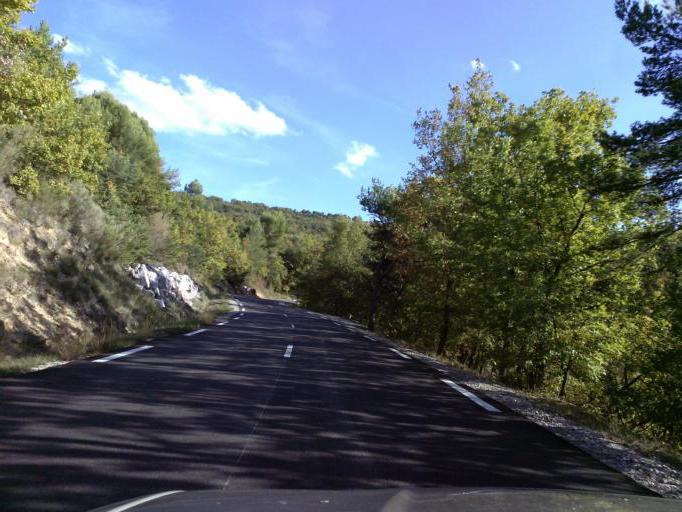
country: FR
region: Provence-Alpes-Cote d'Azur
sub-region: Departement des Alpes-de-Haute-Provence
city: Riez
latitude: 43.9063
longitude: 6.1405
